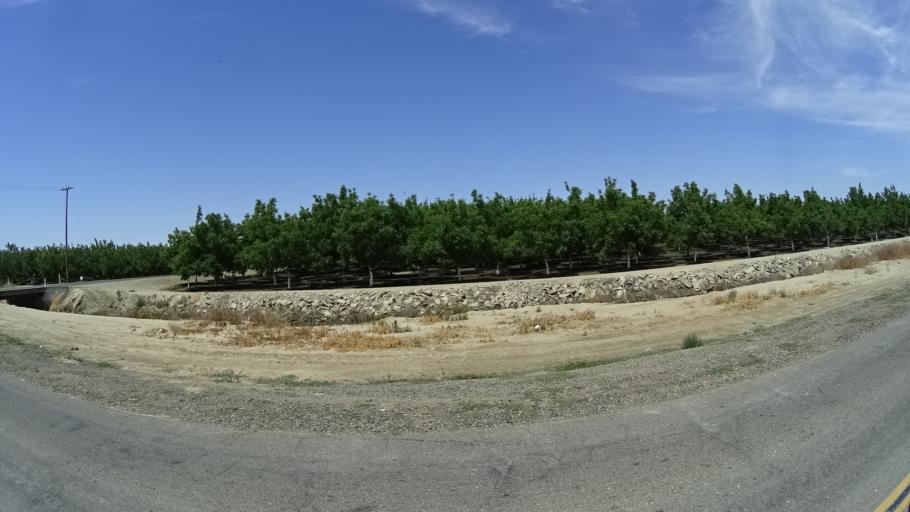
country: US
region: California
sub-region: Kings County
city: Lucerne
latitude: 36.3720
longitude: -119.6910
